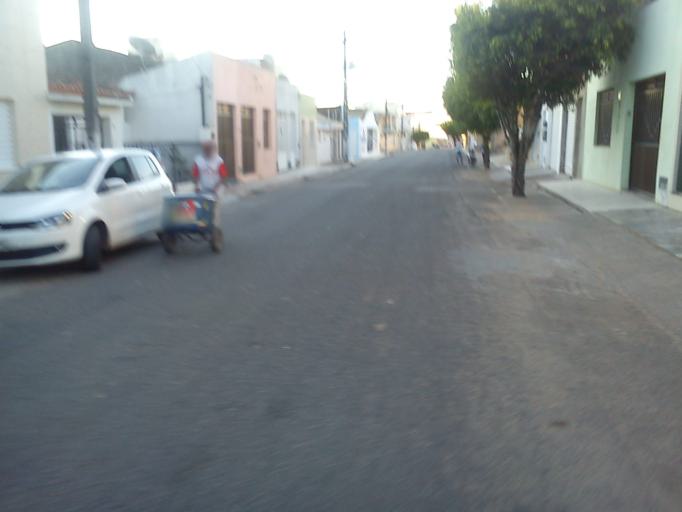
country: BR
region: Sergipe
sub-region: Lagarto
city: Lagarto
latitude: -10.9112
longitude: -37.6763
